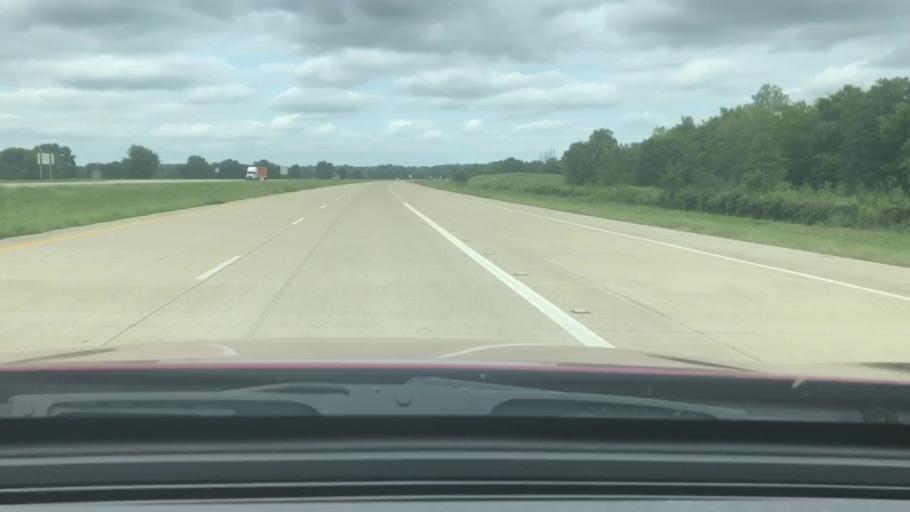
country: US
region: Louisiana
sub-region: Caddo Parish
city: Oil City
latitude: 32.7729
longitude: -93.8888
